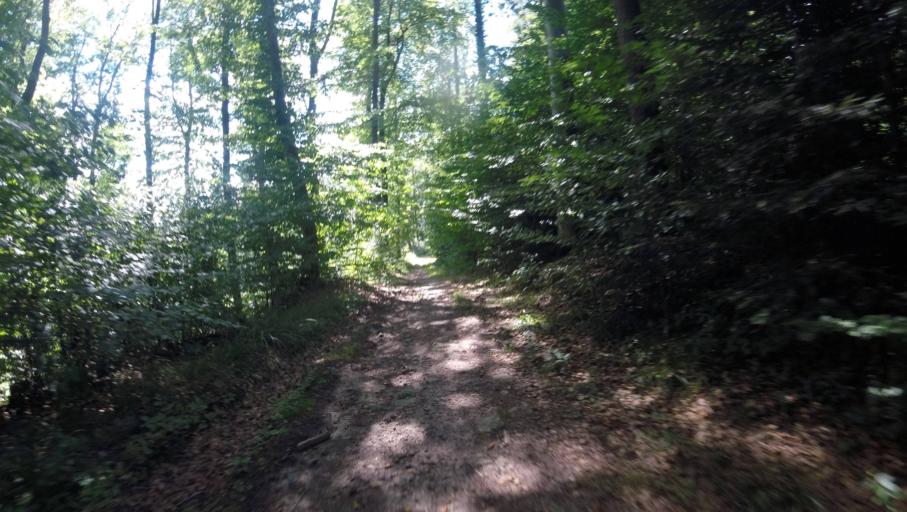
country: DE
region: Baden-Wuerttemberg
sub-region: Regierungsbezirk Stuttgart
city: Spiegelberg
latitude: 49.0096
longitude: 9.4390
